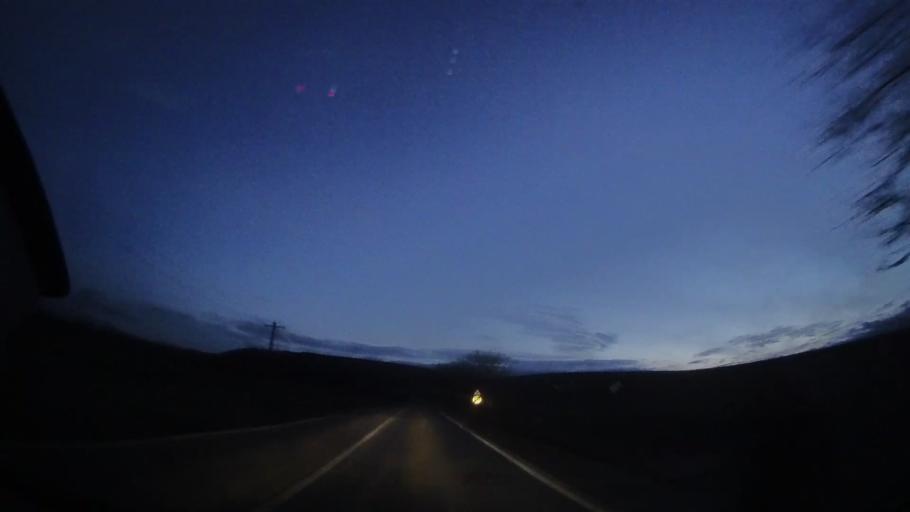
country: RO
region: Mures
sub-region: Comuna Sarmasu
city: Sarmasu
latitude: 46.7774
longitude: 24.2256
